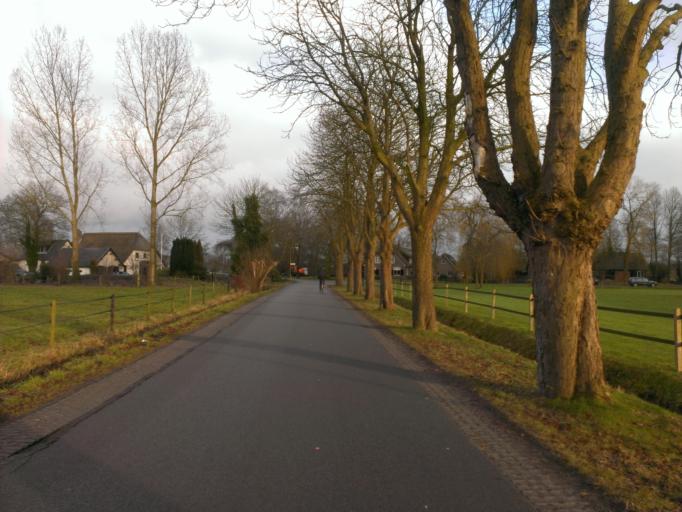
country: NL
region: Gelderland
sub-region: Gemeente Heerde
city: Heerde
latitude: 52.3744
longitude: 6.0293
